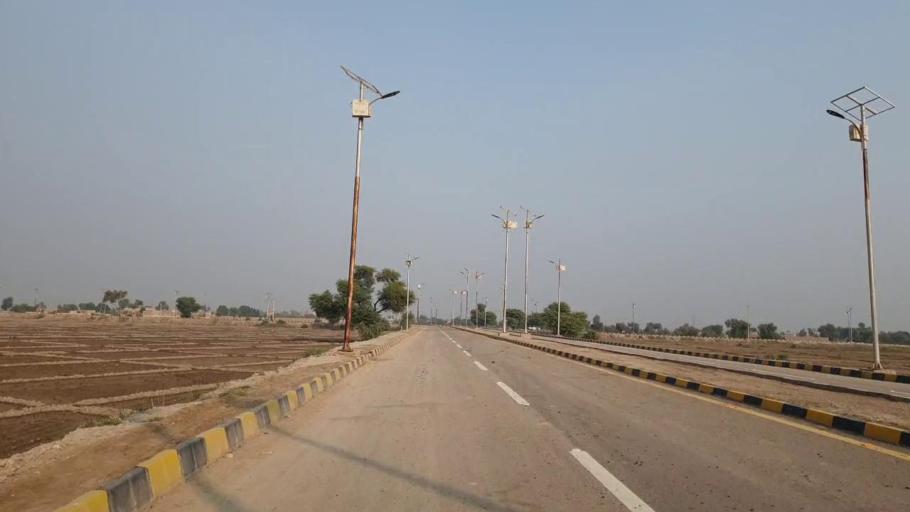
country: PK
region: Sindh
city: Bhan
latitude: 26.4752
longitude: 67.7225
